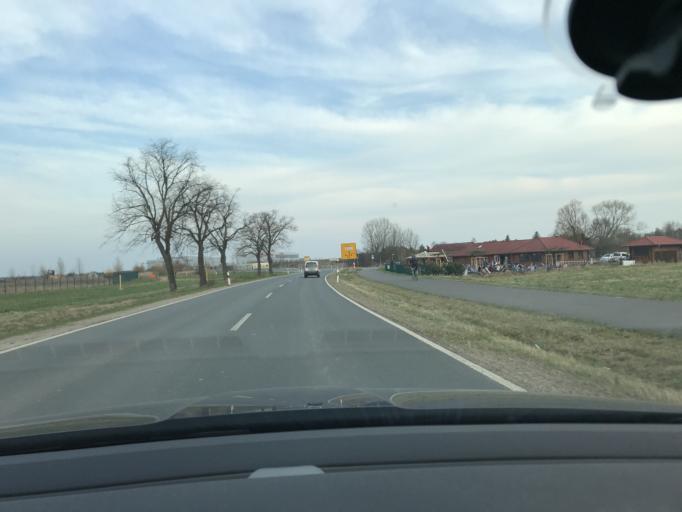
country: DE
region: Brandenburg
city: Schonefeld
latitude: 52.3644
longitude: 13.4717
